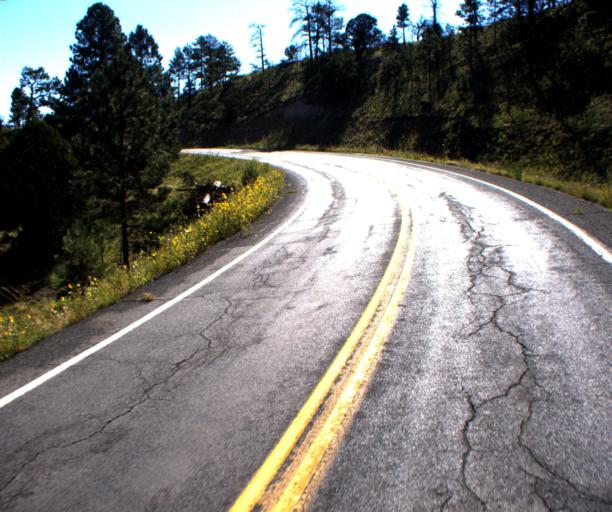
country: US
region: Arizona
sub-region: Apache County
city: Eagar
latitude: 34.0742
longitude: -109.3523
